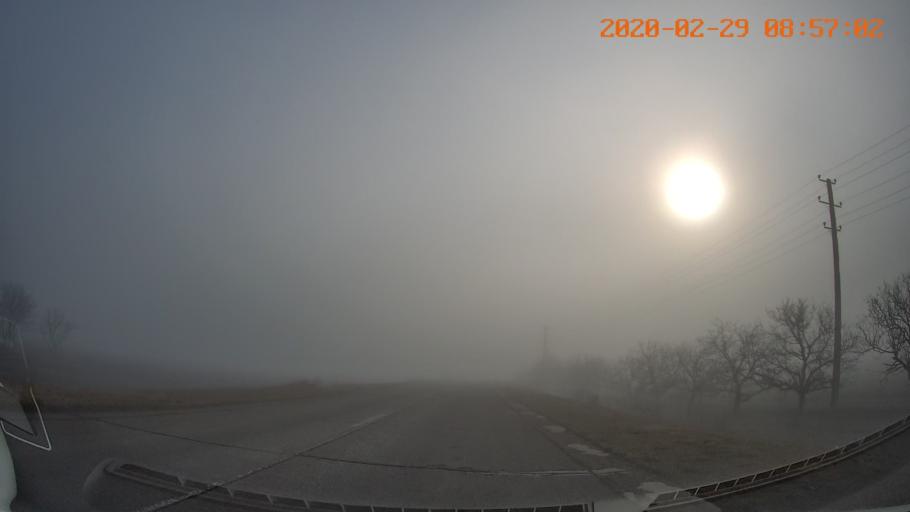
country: MD
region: Telenesti
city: Tiraspolul Nou
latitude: 46.9296
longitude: 29.6196
